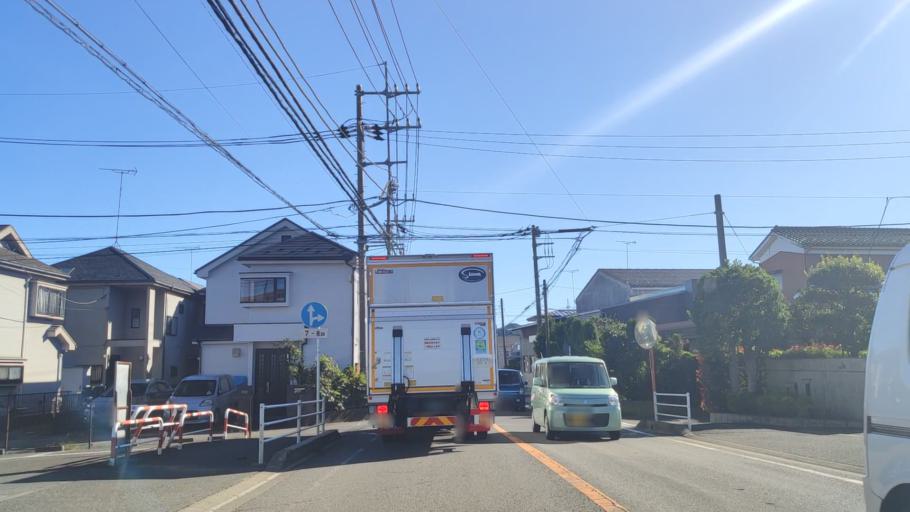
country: JP
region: Tokyo
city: Hachioji
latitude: 35.5939
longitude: 139.3031
